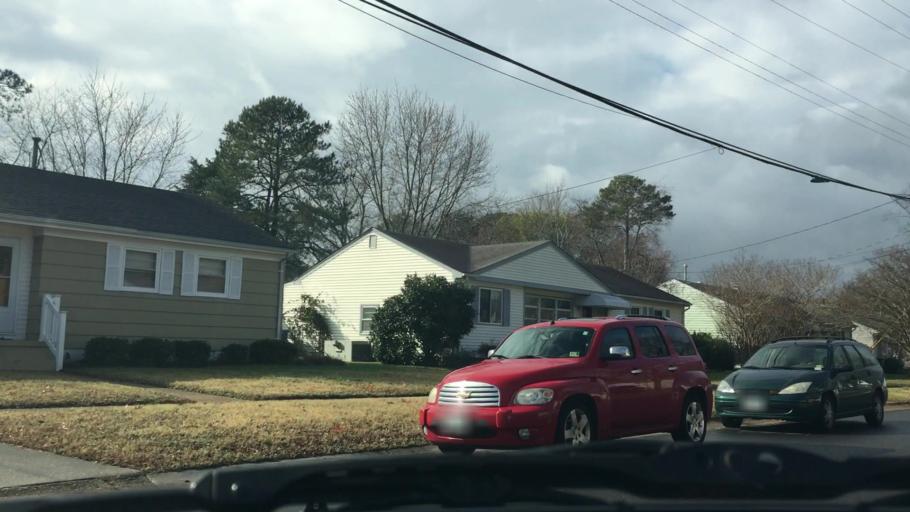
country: US
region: Virginia
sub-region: City of Norfolk
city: Norfolk
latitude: 36.9287
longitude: -76.2319
